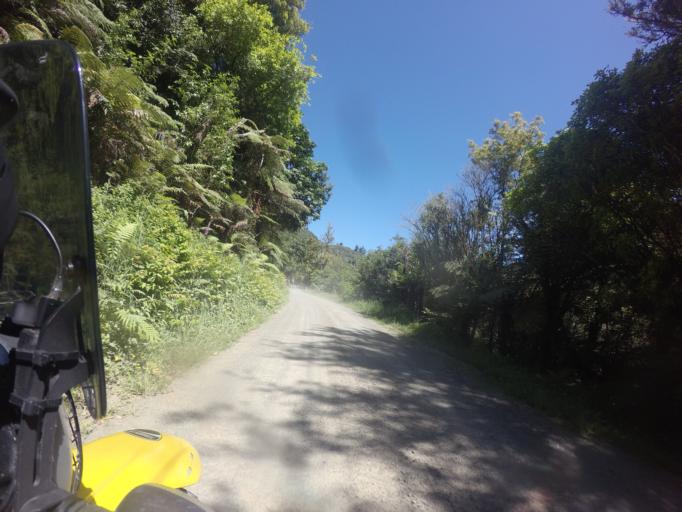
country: NZ
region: Bay of Plenty
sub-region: Opotiki District
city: Opotiki
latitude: -38.2838
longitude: 177.3421
